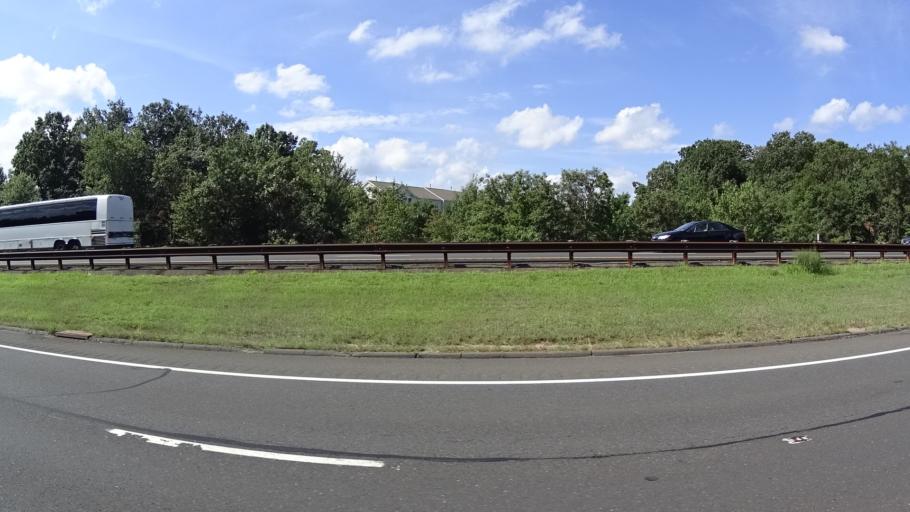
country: US
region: New Jersey
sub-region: Middlesex County
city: South Amboy
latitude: 40.4590
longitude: -74.2780
